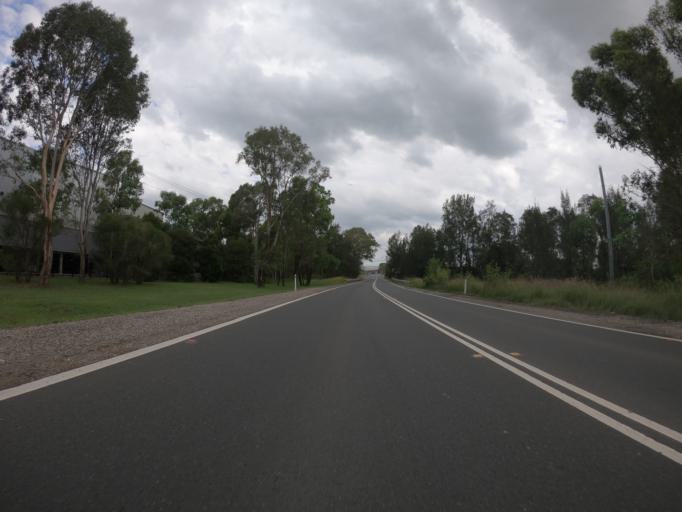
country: AU
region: New South Wales
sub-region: Blacktown
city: Mount Druitt
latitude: -33.8131
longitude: 150.7758
